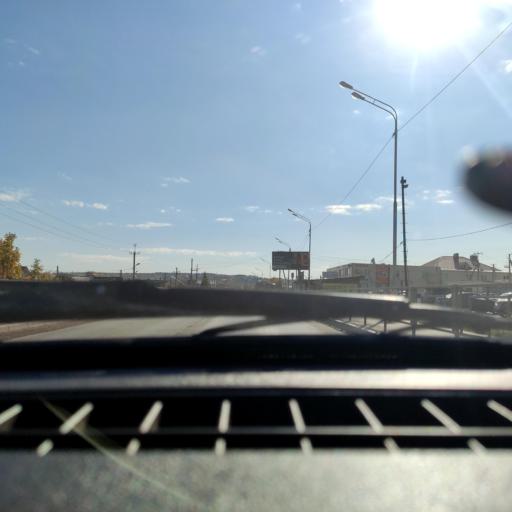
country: RU
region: Bashkortostan
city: Ufa
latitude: 54.6161
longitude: 55.9338
